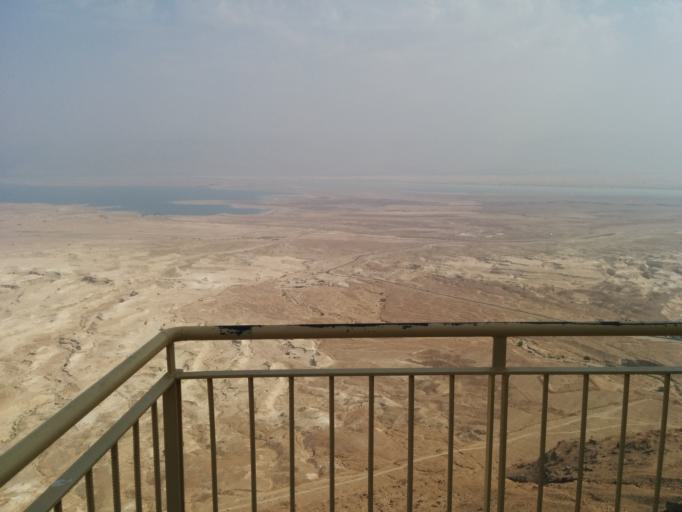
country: IL
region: Southern District
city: `En Boqeq
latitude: 31.3186
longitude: 35.3543
